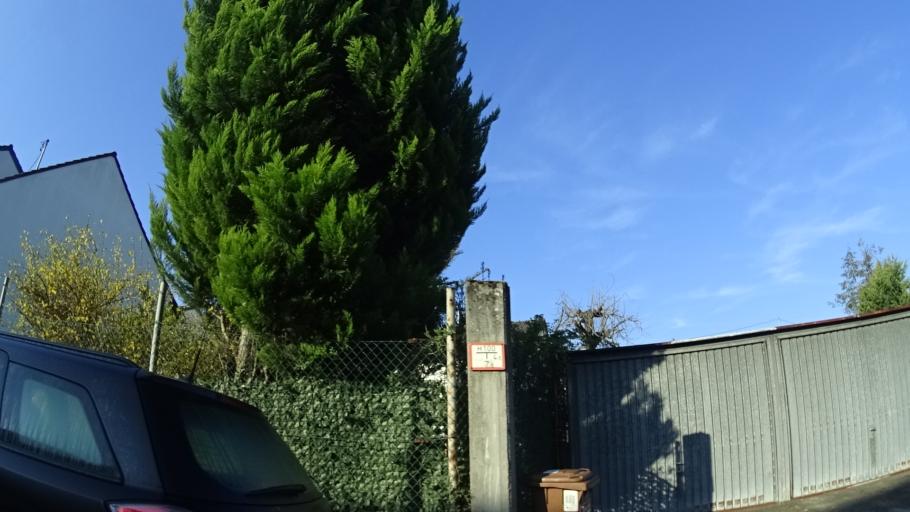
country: DE
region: Baden-Wuerttemberg
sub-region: Karlsruhe Region
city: Leimen
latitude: 49.3765
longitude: 8.6697
